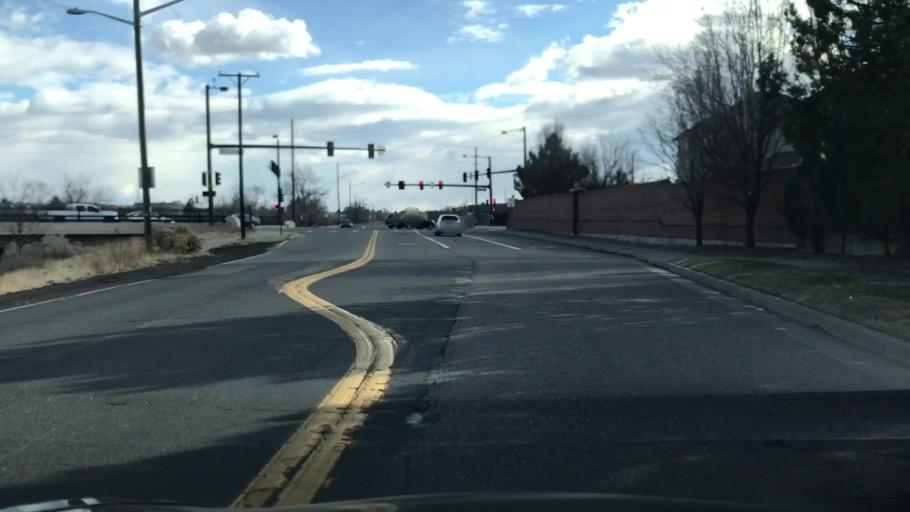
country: US
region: Colorado
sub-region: Arapahoe County
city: Glendale
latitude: 39.6855
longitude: -104.9044
